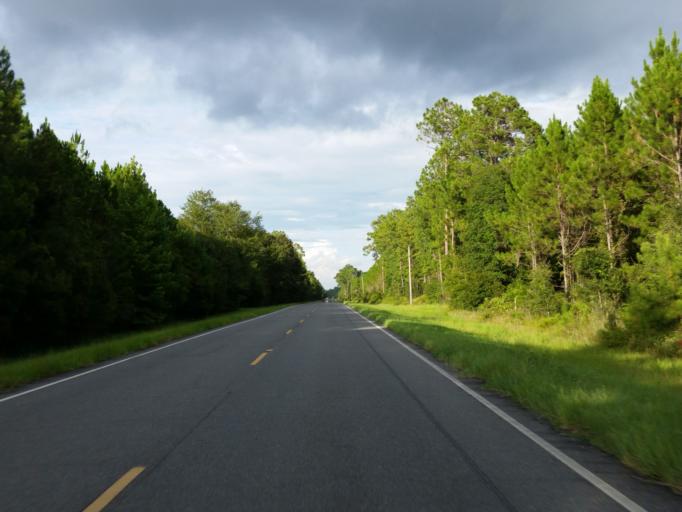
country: US
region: Florida
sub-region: Hamilton County
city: Jasper
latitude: 30.6311
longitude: -82.5978
